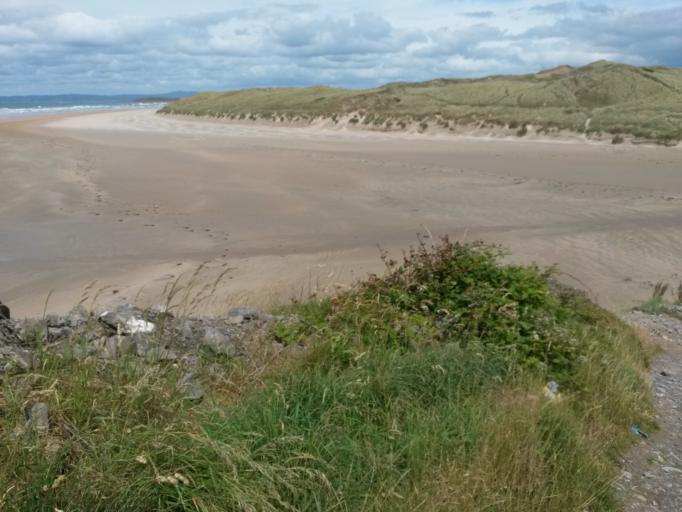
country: IE
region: Ulster
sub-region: County Donegal
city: Bundoran
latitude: 54.4905
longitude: -8.2658
